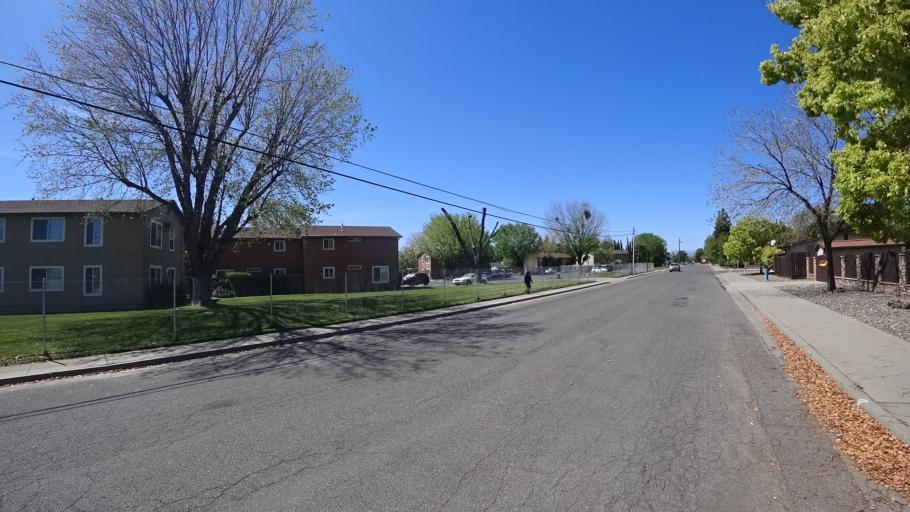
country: US
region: California
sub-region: Glenn County
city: Orland
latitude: 39.7510
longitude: -122.1796
